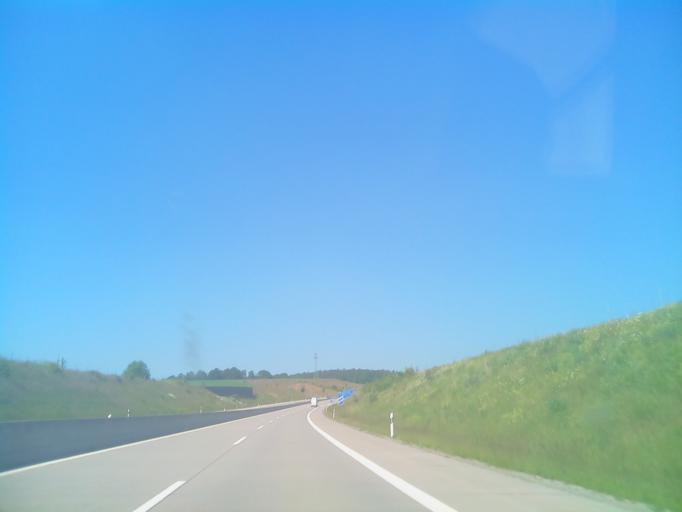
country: DE
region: Bavaria
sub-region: Regierungsbezirk Unterfranken
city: Rodelmaier
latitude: 50.3238
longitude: 10.2888
